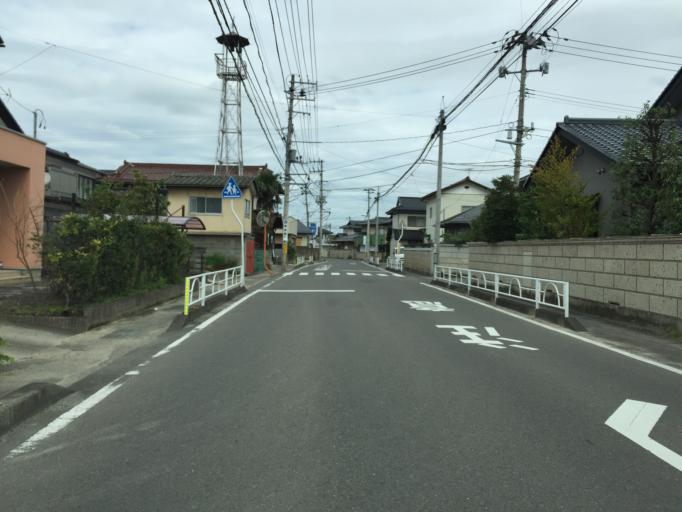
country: JP
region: Fukushima
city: Hobaramachi
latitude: 37.8130
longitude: 140.4961
